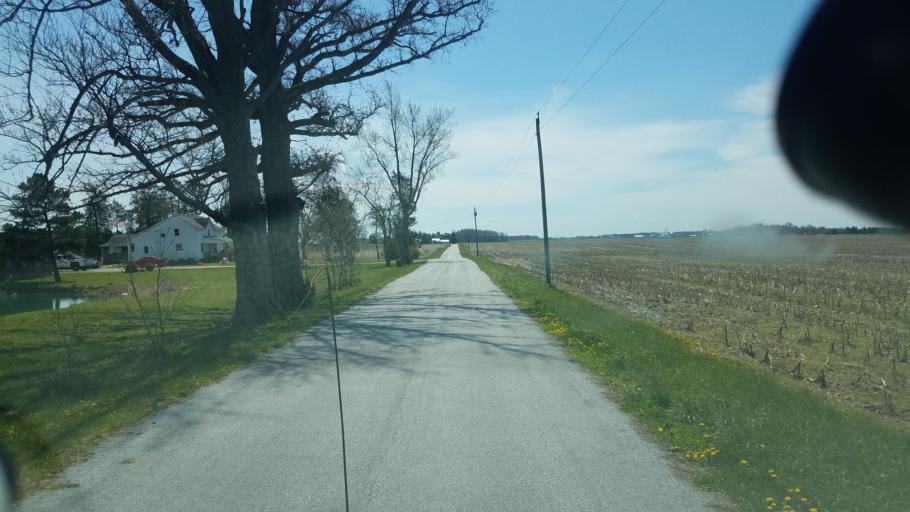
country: US
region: Ohio
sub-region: Hardin County
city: Kenton
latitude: 40.6796
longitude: -83.5051
